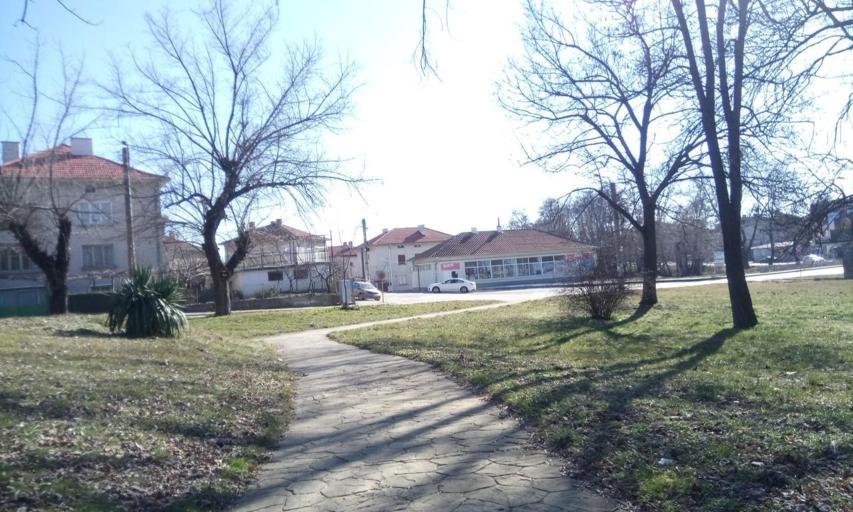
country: BG
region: Plovdiv
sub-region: Obshtina Khisarya
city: Khisarya
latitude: 42.5092
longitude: 24.7139
